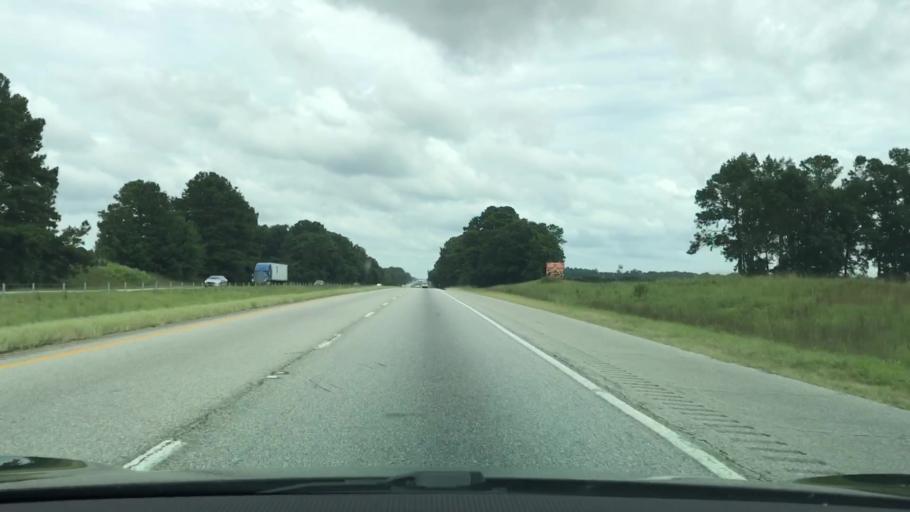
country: US
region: Alabama
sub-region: Chambers County
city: Huguley
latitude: 32.7966
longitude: -85.2352
